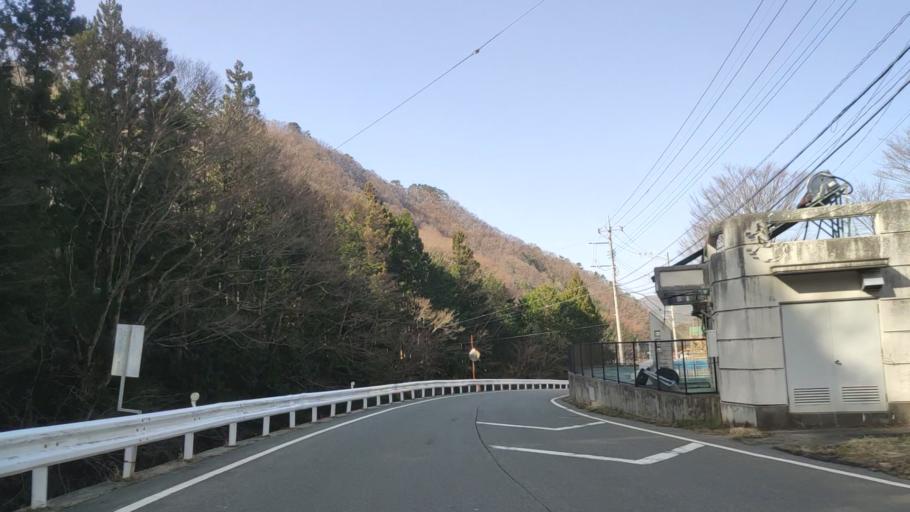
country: JP
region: Yamanashi
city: Fujikawaguchiko
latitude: 35.5545
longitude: 138.6711
